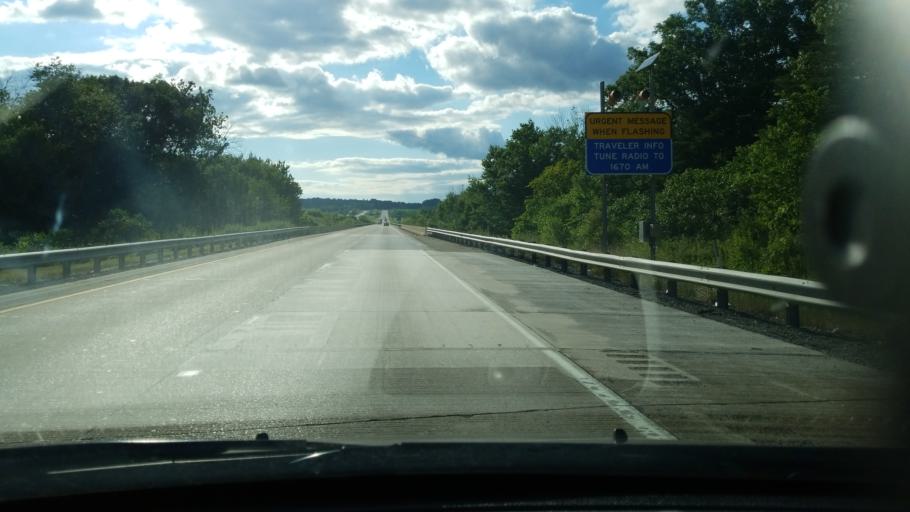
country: US
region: Pennsylvania
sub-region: Northumberland County
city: Milton
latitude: 41.0051
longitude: -76.7594
